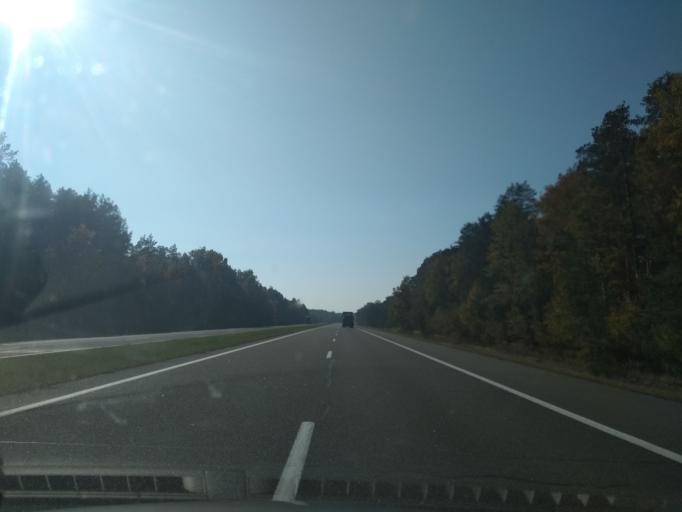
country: BY
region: Brest
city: Antopal'
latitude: 52.3729
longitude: 24.7466
